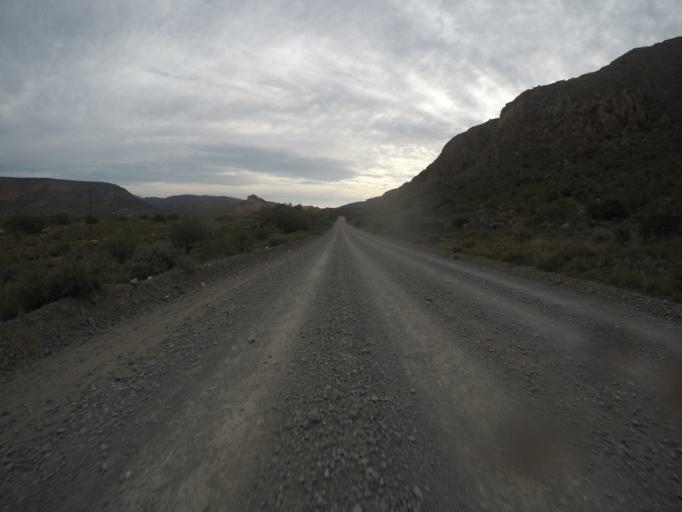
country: ZA
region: Eastern Cape
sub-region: Cacadu District Municipality
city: Willowmore
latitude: -33.5195
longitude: 23.6856
